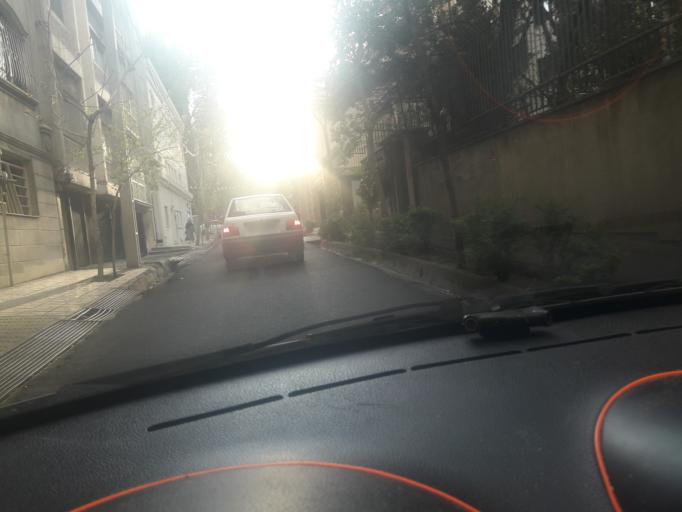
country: IR
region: Tehran
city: Tehran
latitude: 35.7414
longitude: 51.4060
